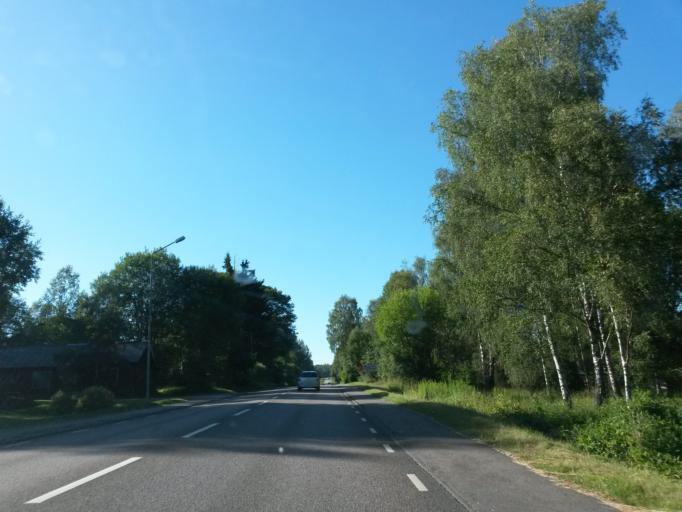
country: SE
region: Vaestra Goetaland
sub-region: Boras Kommun
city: Boras
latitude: 57.8284
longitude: 12.9968
